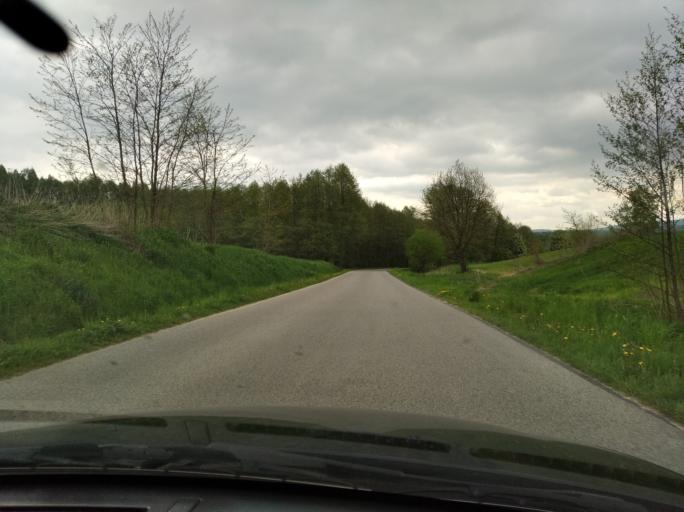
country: PL
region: Subcarpathian Voivodeship
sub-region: Powiat debicki
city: Leki Gorne
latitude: 49.9822
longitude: 21.1539
